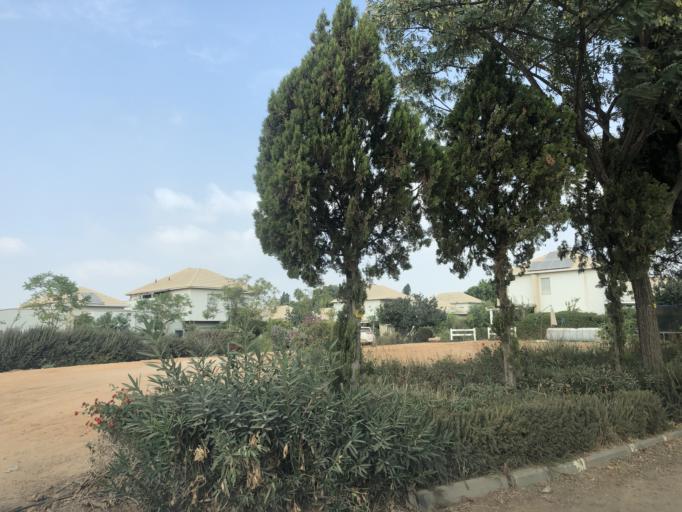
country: IL
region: Central District
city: Rosh Ha'Ayin
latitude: 32.0805
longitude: 34.9354
